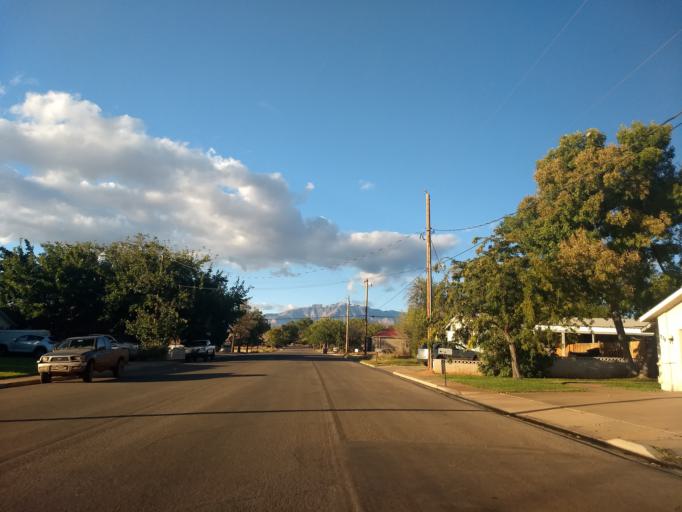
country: US
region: Utah
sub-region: Washington County
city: Washington
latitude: 37.1351
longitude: -113.5081
